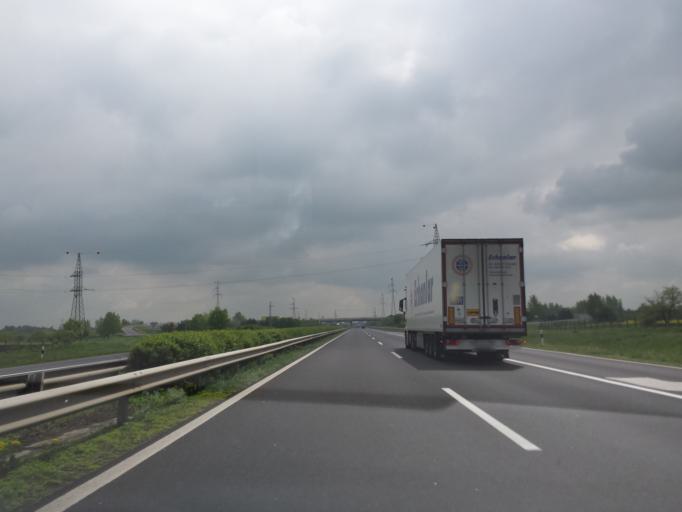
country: HU
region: Gyor-Moson-Sopron
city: Mosonmagyarovar
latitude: 47.8548
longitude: 17.2438
